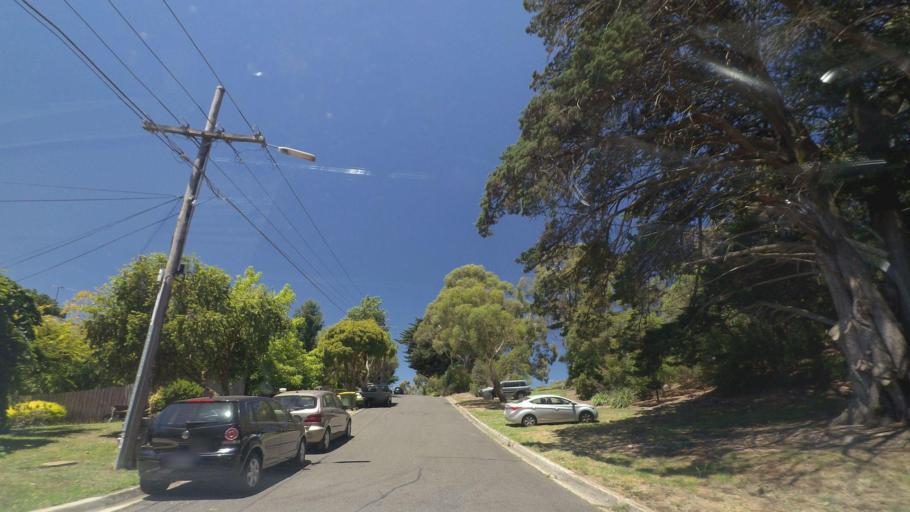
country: AU
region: Victoria
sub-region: Yarra Ranges
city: Chirnside Park
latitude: -37.7594
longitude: 145.3268
